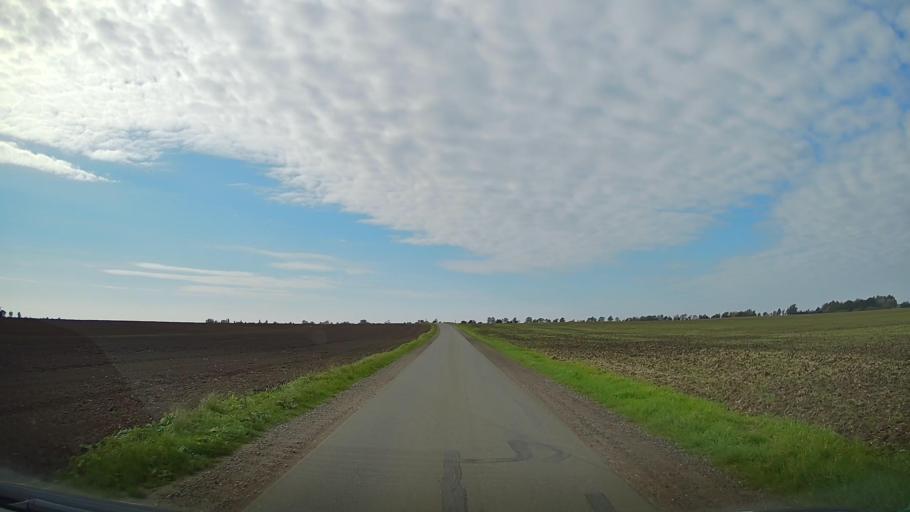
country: DE
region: Schleswig-Holstein
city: Grossenbrode
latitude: 54.4968
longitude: 11.0521
